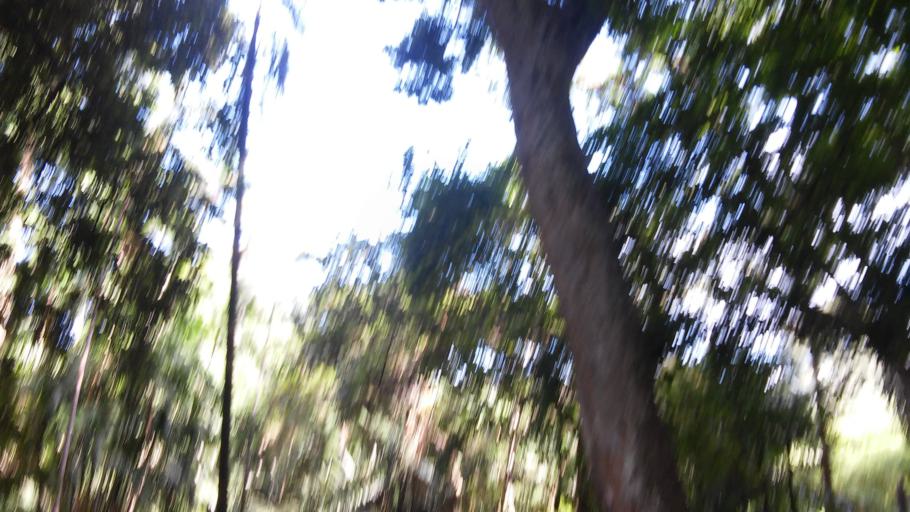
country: LK
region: Central
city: Kandy
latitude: 7.2669
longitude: 80.5949
